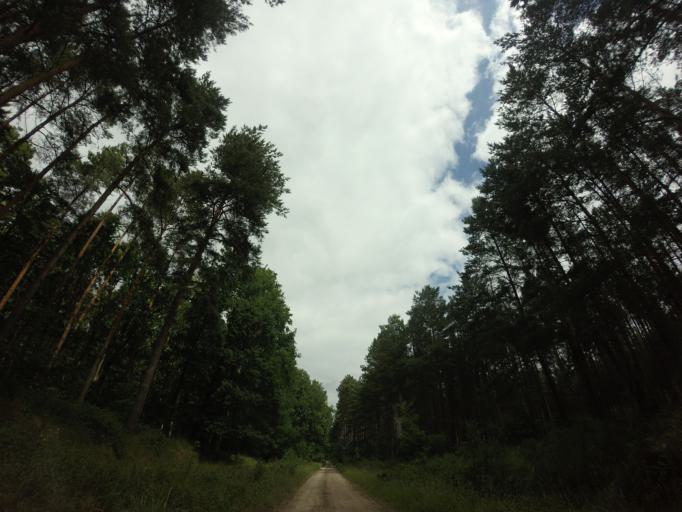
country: PL
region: West Pomeranian Voivodeship
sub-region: Powiat choszczenski
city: Krzecin
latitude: 53.0176
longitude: 15.5296
